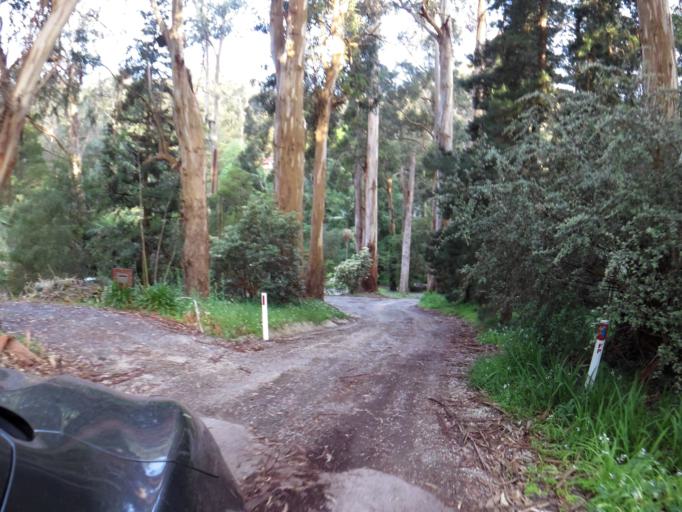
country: AU
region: Victoria
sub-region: Yarra Ranges
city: Belgrave
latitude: -37.8972
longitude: 145.3460
